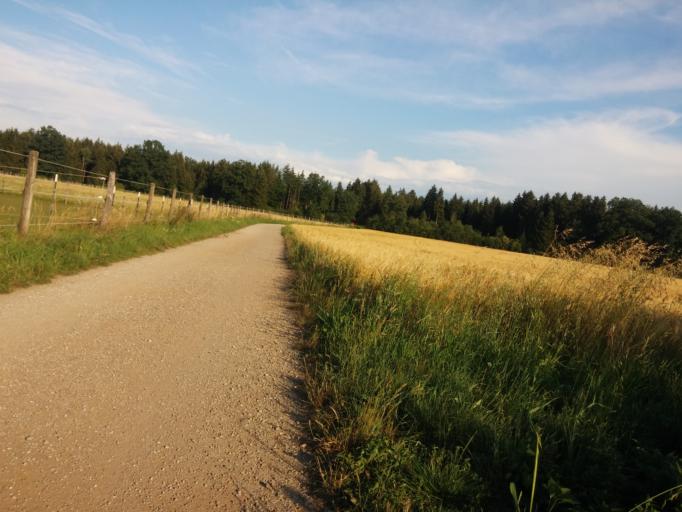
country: DE
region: Bavaria
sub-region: Upper Bavaria
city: Grasbrunn
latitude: 48.0727
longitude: 11.7533
